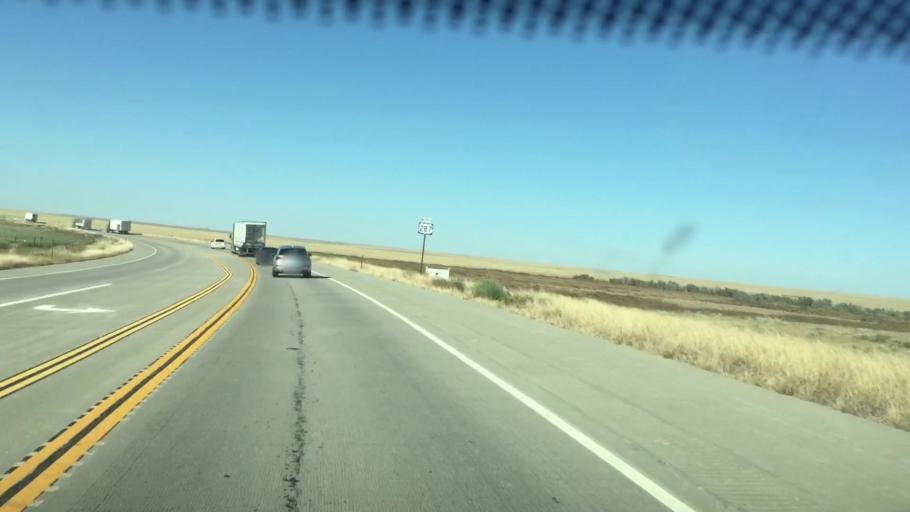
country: US
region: Colorado
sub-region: Kiowa County
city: Eads
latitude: 38.3488
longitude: -102.7142
